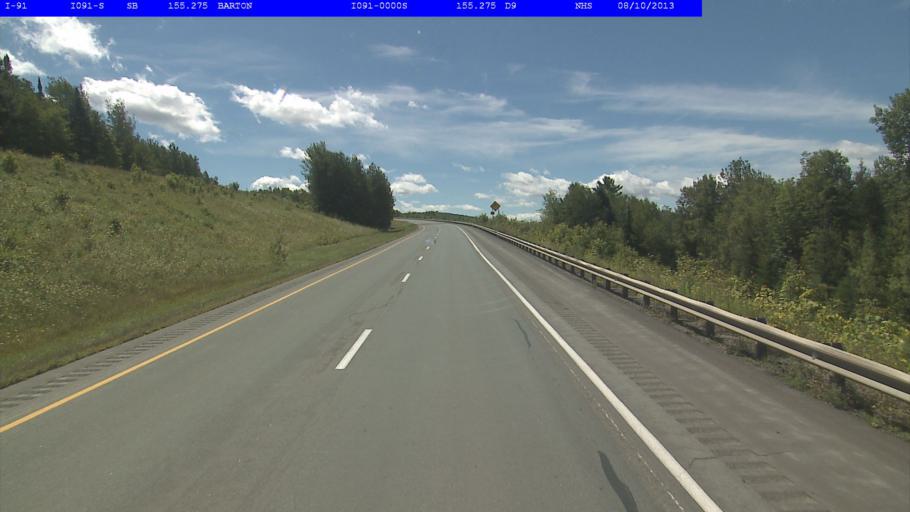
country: US
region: Vermont
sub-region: Orleans County
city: Newport
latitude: 44.7264
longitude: -72.1806
